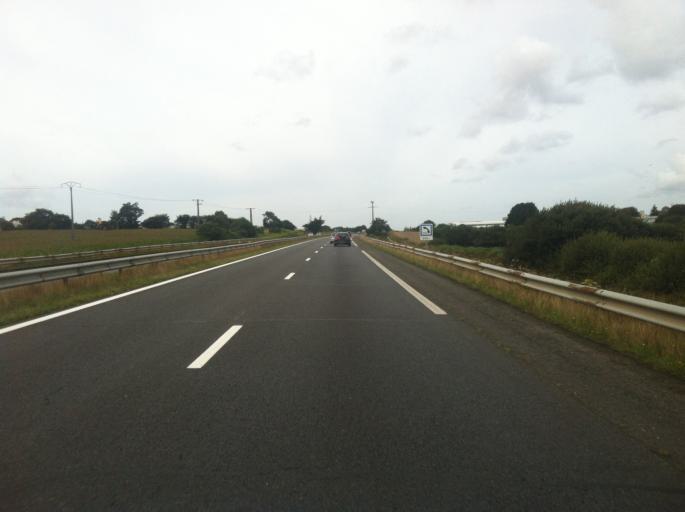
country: FR
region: Brittany
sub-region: Departement du Finistere
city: Guipavas
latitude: 48.4434
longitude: -4.4030
